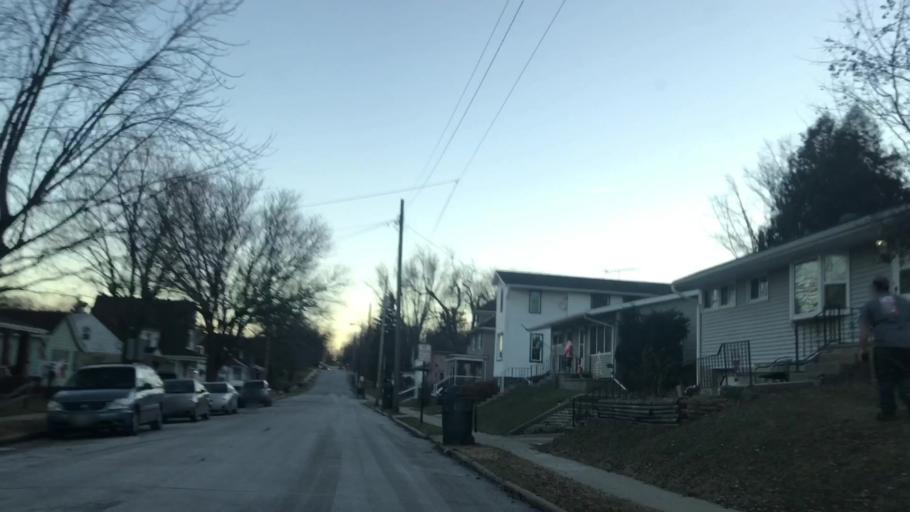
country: US
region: Wisconsin
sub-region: Dodge County
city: Mayville
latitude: 43.5003
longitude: -88.5525
